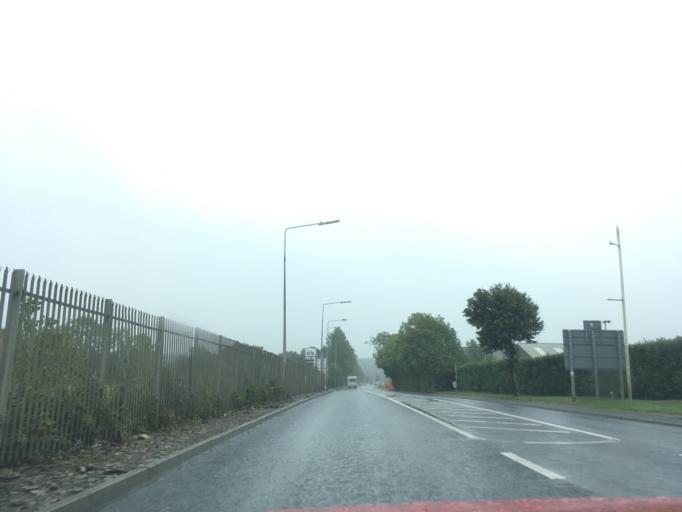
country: IE
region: Leinster
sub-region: Loch Garman
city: New Ross
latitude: 52.3897
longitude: -6.9296
